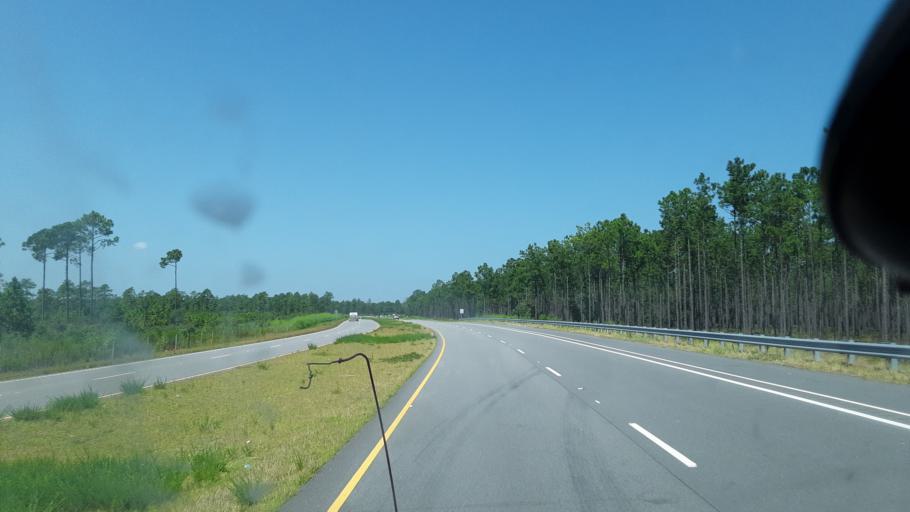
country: US
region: South Carolina
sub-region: Horry County
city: Forestbrook
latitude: 33.8030
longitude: -78.8862
